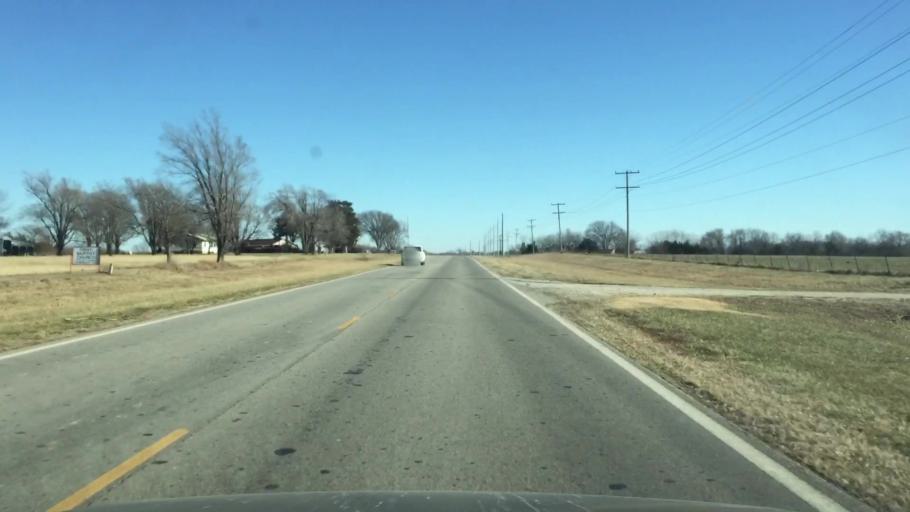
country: US
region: Kansas
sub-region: Allen County
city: Humboldt
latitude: 37.8201
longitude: -95.4249
